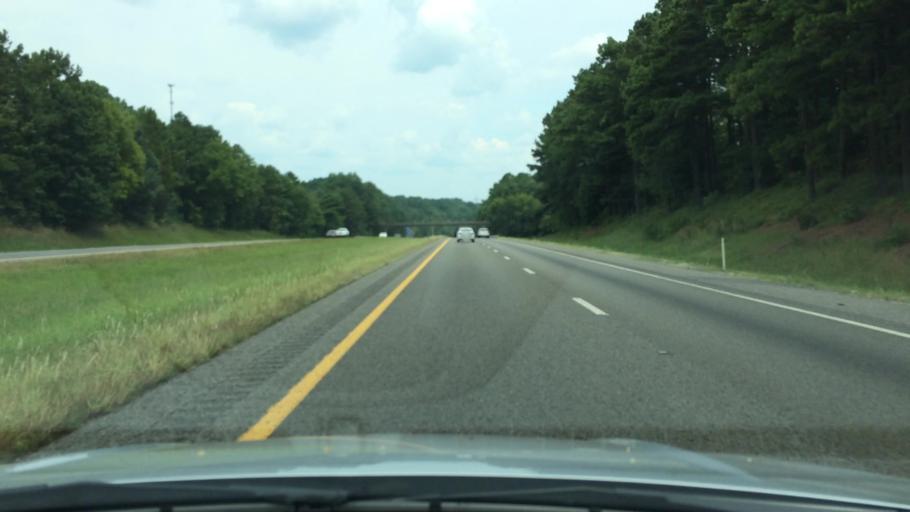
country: US
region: Tennessee
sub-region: Marshall County
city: Cornersville
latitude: 35.3950
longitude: -86.8790
